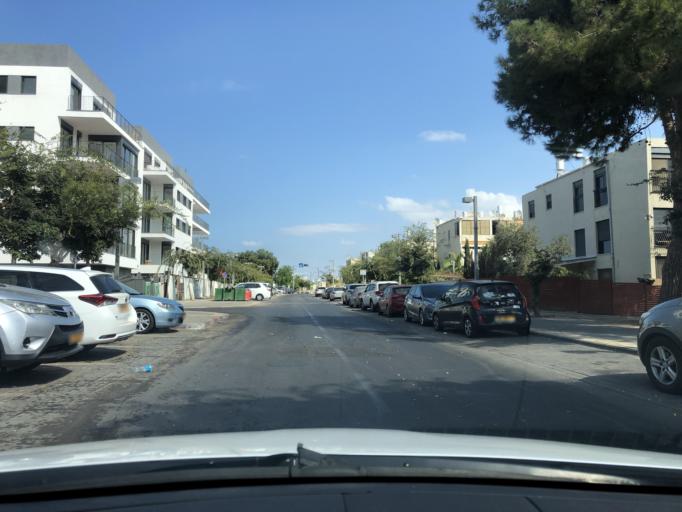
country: IL
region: Tel Aviv
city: Yafo
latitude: 32.0398
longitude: 34.7552
